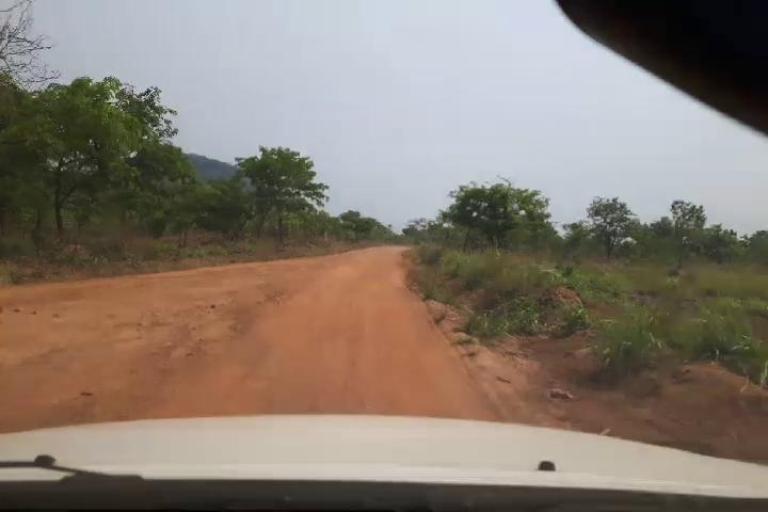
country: SL
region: Northern Province
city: Bumbuna
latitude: 8.8902
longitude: -11.8183
